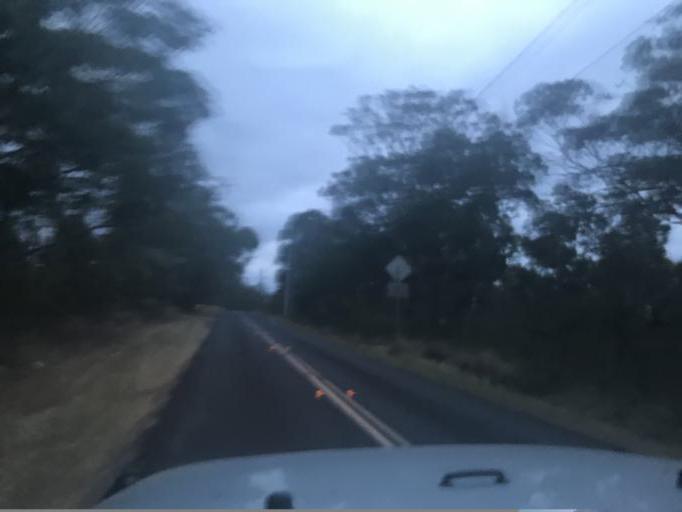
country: AU
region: New South Wales
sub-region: Hawkesbury
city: Pitt Town
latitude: -33.4703
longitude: 150.8561
